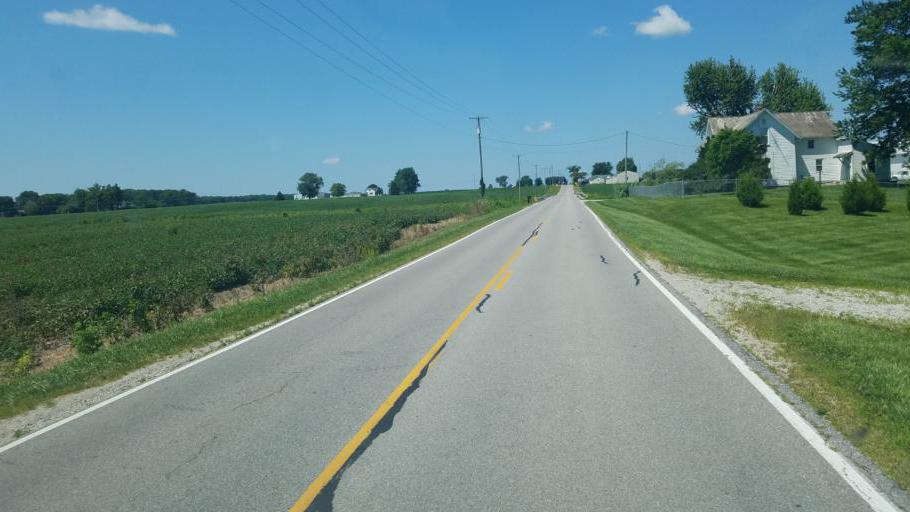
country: US
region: Ohio
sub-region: Marion County
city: Prospect
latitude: 40.4841
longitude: -83.0808
